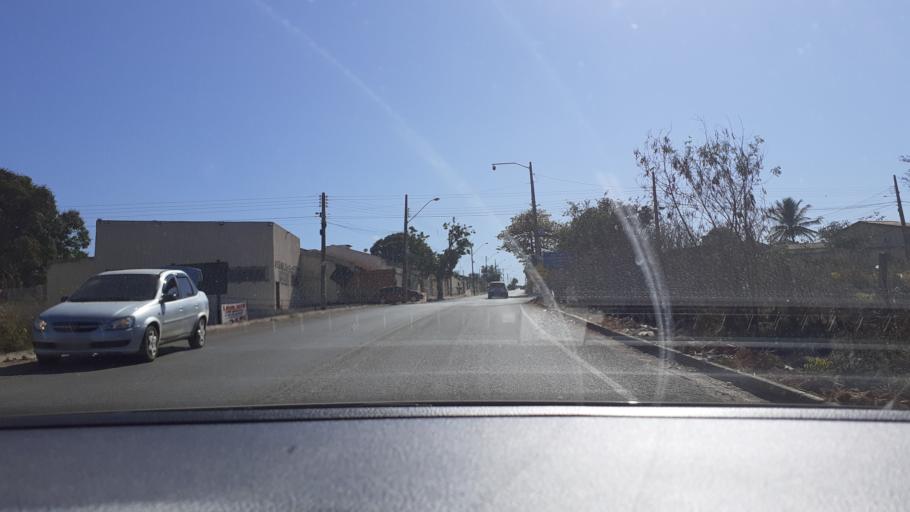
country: BR
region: Goias
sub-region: Aparecida De Goiania
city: Aparecida de Goiania
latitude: -16.8452
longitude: -49.2525
